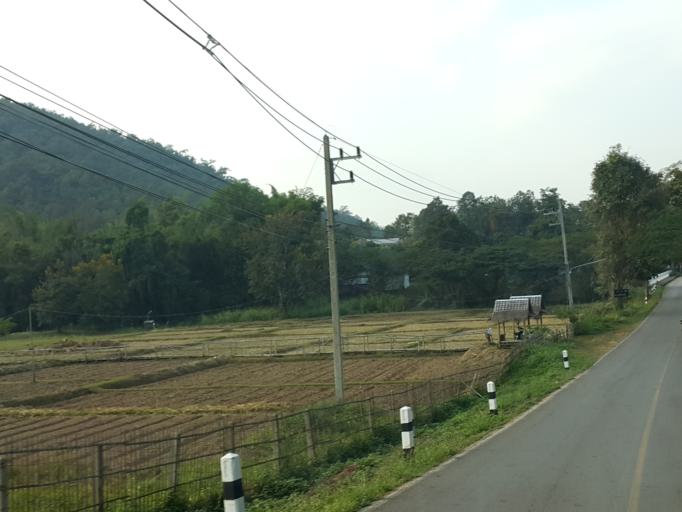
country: TH
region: Chiang Mai
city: Mae On
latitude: 18.8970
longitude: 99.2600
